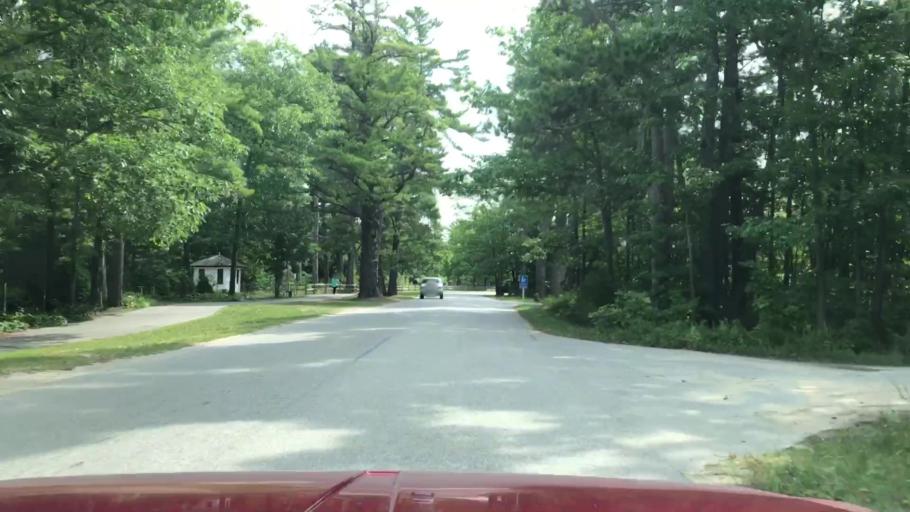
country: US
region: Michigan
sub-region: Charlevoix County
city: Charlevoix
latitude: 45.7468
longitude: -85.5241
